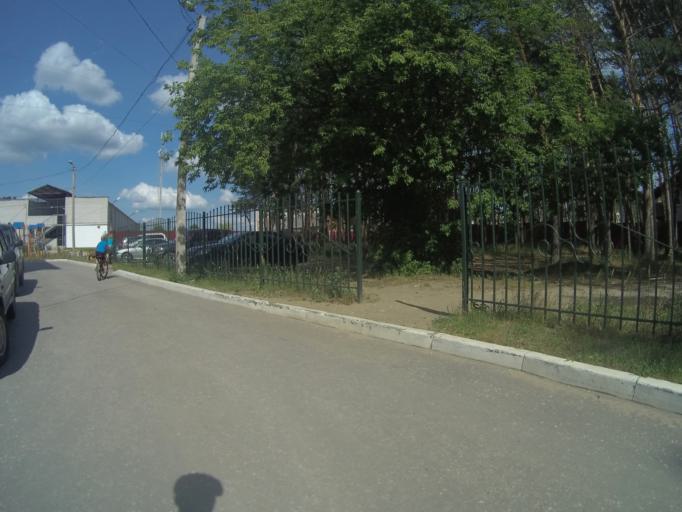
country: RU
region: Vladimir
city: Kommunar
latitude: 56.1074
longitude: 40.4364
